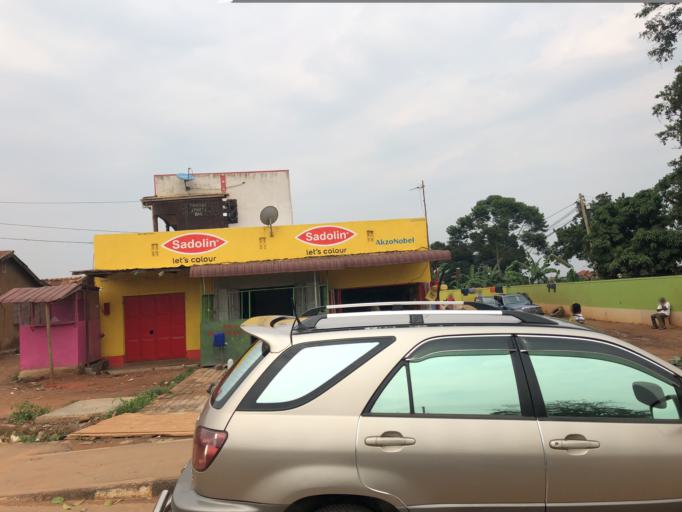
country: UG
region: Central Region
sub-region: Mukono District
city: Mukono
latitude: 0.3710
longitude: 32.7552
